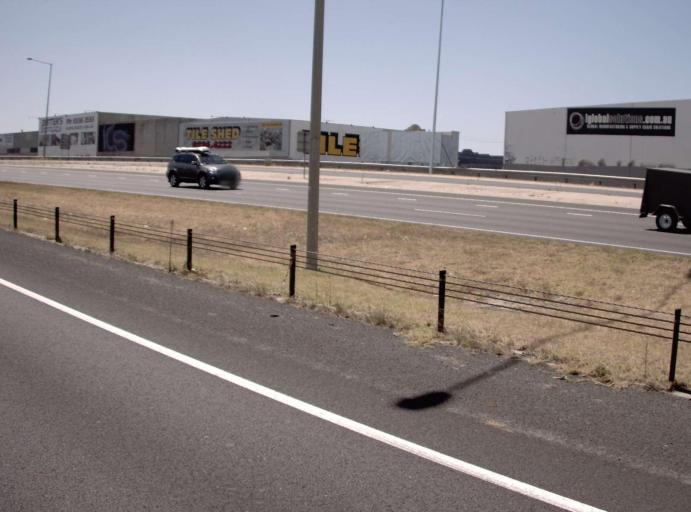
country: AU
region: Victoria
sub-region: Moonee Valley
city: Keilor East
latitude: -37.7370
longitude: 144.8519
